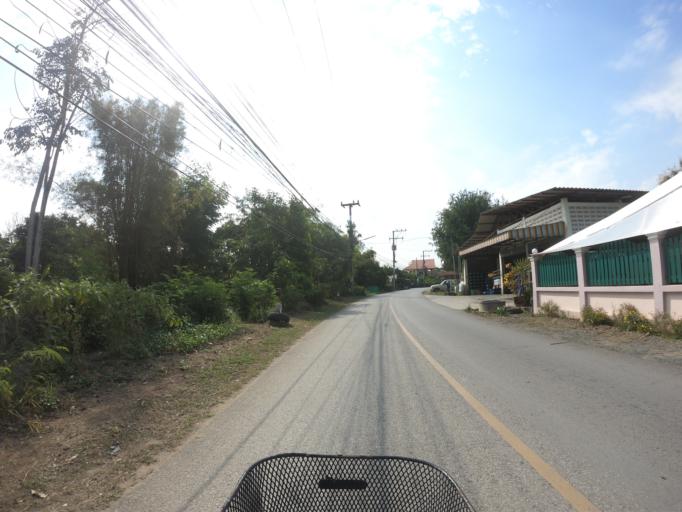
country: TH
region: Chiang Mai
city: Saraphi
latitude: 18.7062
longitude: 99.0610
